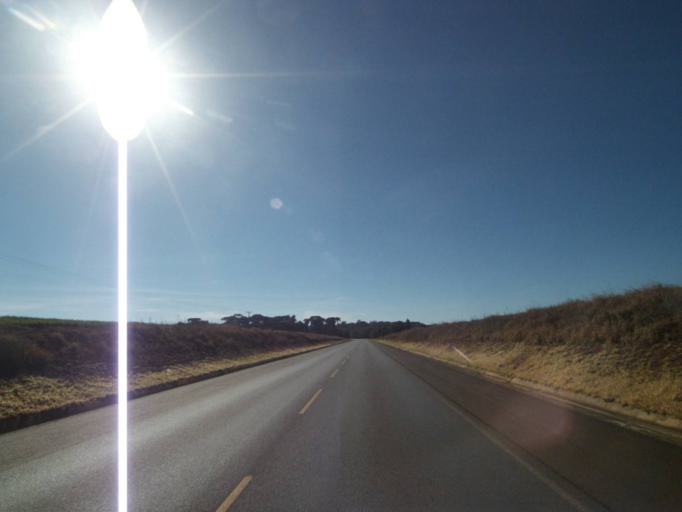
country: BR
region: Parana
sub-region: Tibagi
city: Tibagi
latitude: -24.4282
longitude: -50.4024
